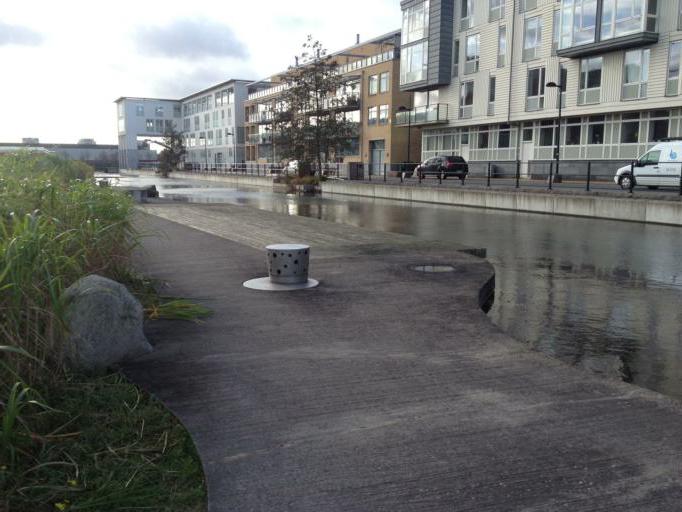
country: SE
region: Skane
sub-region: Malmo
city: Malmoe
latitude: 55.6112
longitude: 12.9758
